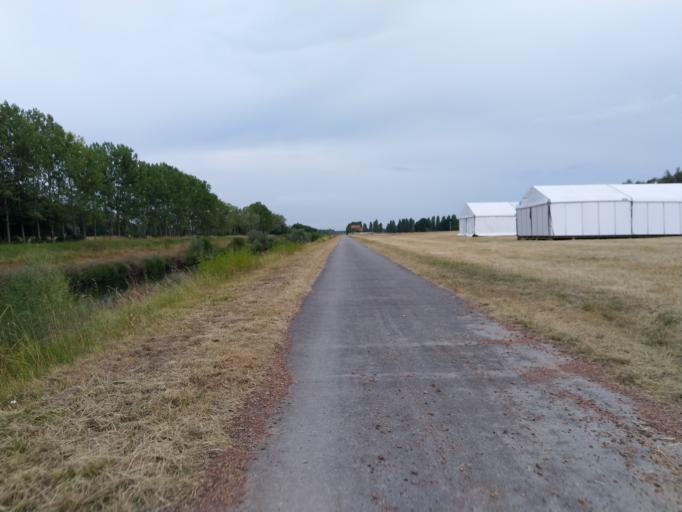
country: BE
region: Wallonia
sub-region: Province du Hainaut
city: Hensies
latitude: 50.4497
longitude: 3.7057
